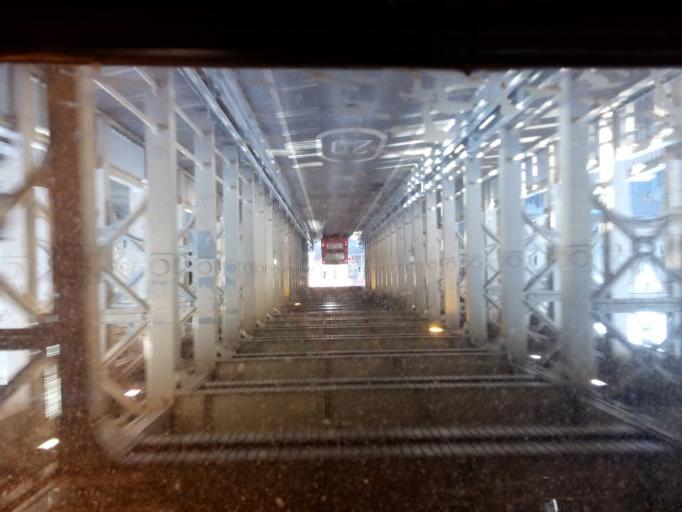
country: GB
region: England
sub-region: Newcastle upon Tyne
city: Newcastle upon Tyne
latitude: 54.9671
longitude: -1.6088
